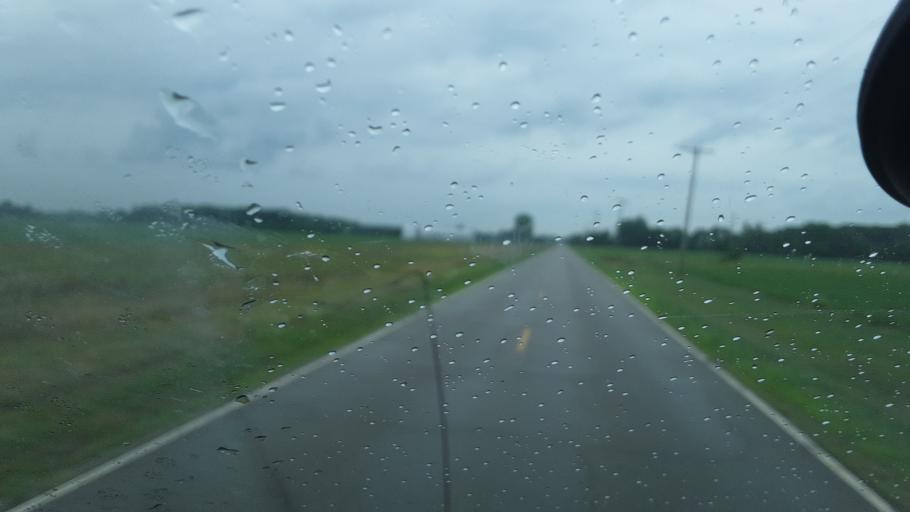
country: US
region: Ohio
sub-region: Williams County
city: Bryan
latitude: 41.3557
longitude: -84.6307
